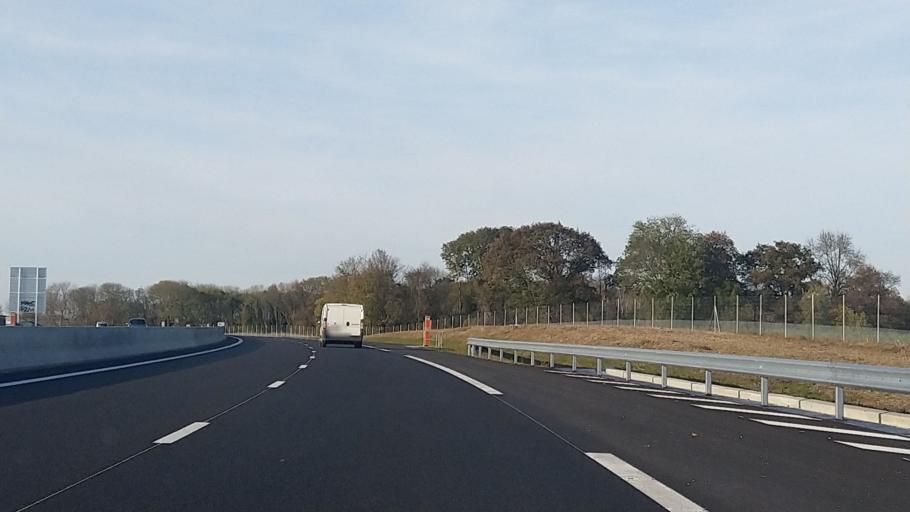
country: FR
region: Ile-de-France
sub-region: Departement du Val-d'Oise
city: Montsoult
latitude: 49.0789
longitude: 2.3313
